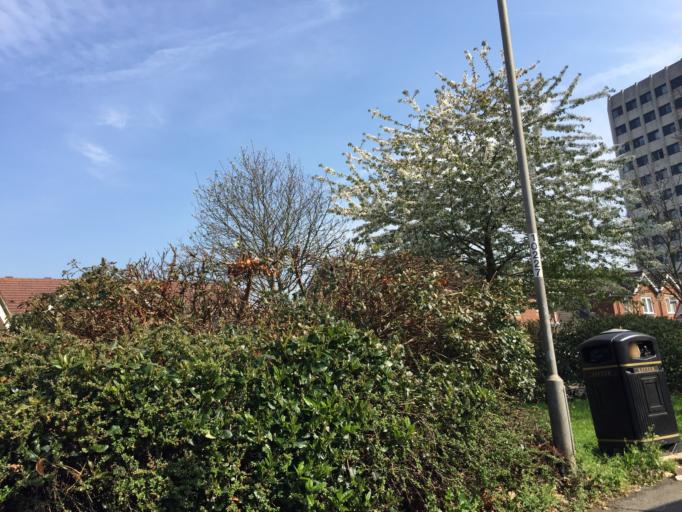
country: GB
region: England
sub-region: Essex
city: Harlow
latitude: 51.7691
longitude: 0.0893
